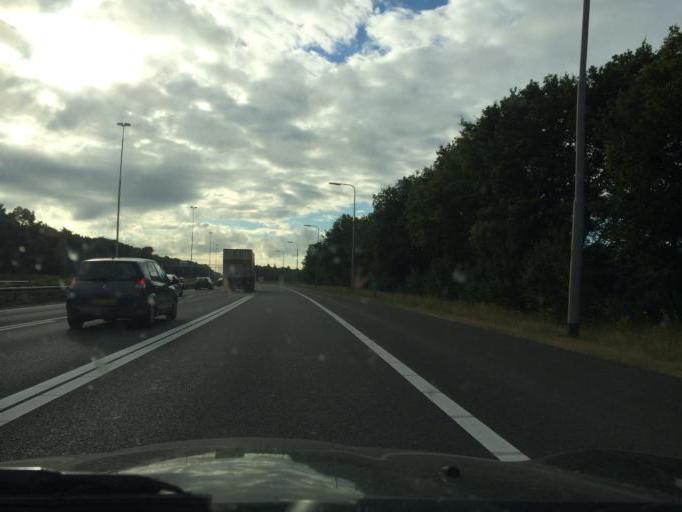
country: NL
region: North Brabant
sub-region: Gemeente Oirschot
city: Oirschot
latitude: 51.4930
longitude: 5.3139
